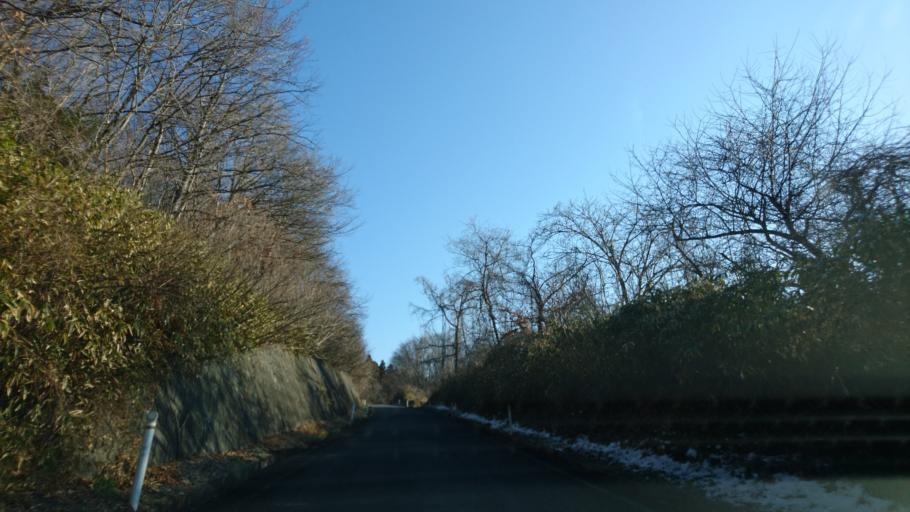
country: JP
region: Iwate
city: Ichinoseki
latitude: 38.9170
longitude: 141.2853
